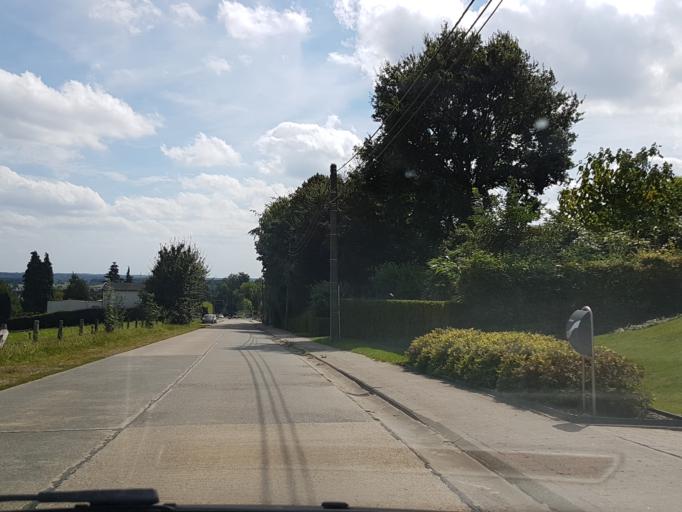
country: BE
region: Flanders
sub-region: Provincie Vlaams-Brabant
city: Bertem
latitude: 50.8788
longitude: 4.6270
